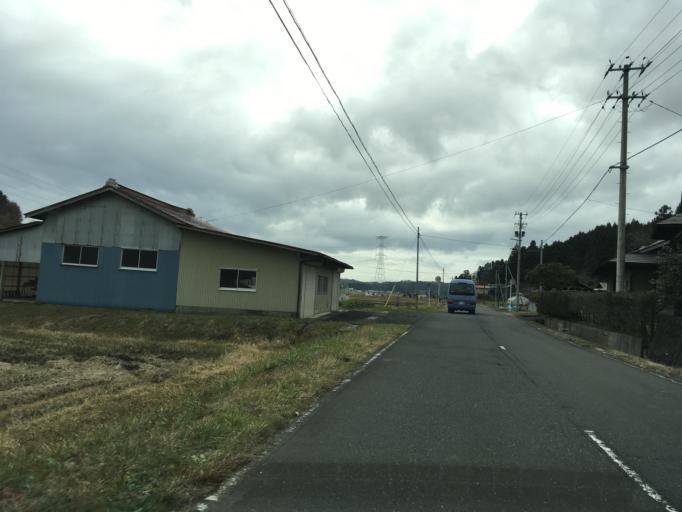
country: JP
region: Iwate
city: Ichinoseki
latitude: 38.8255
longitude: 141.0476
